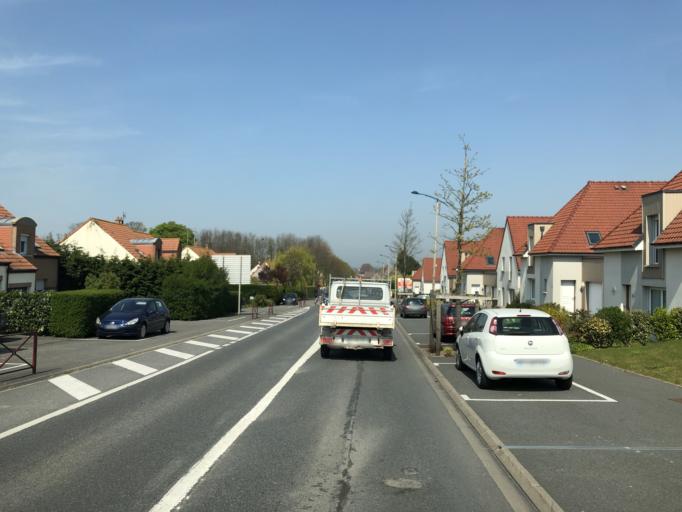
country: FR
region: Nord-Pas-de-Calais
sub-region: Departement du Pas-de-Calais
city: Coquelles
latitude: 50.9302
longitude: 1.7984
